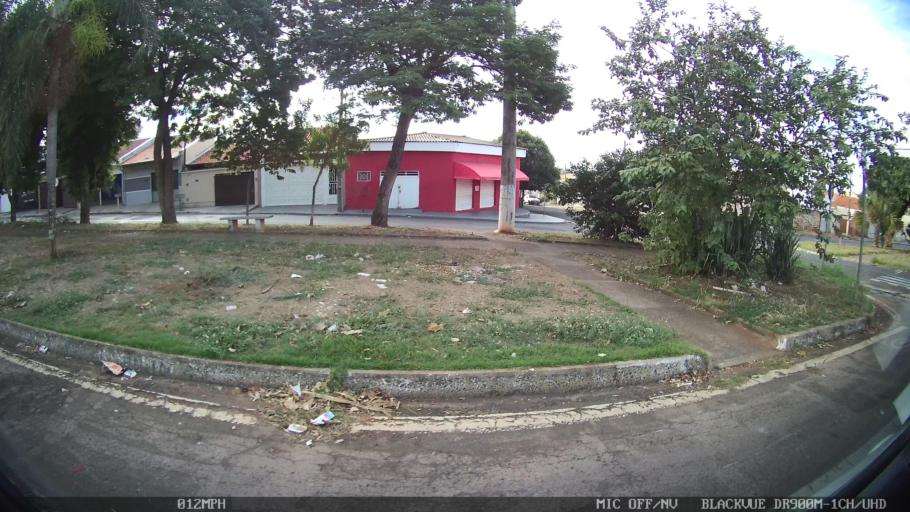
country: BR
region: Sao Paulo
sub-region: Catanduva
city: Catanduva
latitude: -21.1250
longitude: -48.9967
